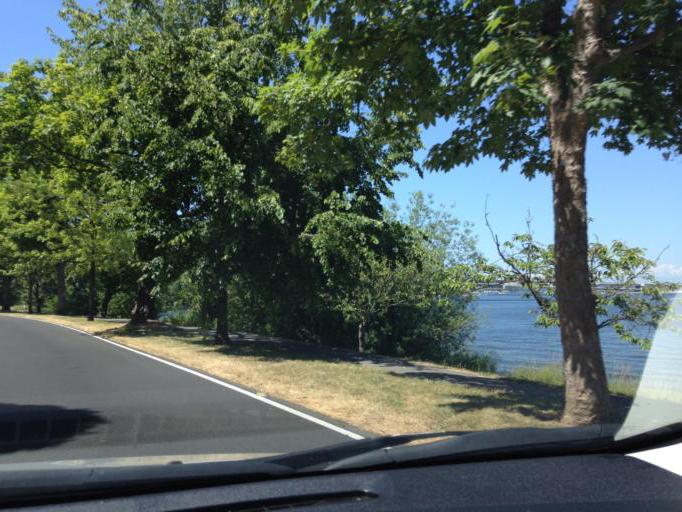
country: US
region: Washington
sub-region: King County
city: Seattle
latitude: 47.5816
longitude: -122.2855
